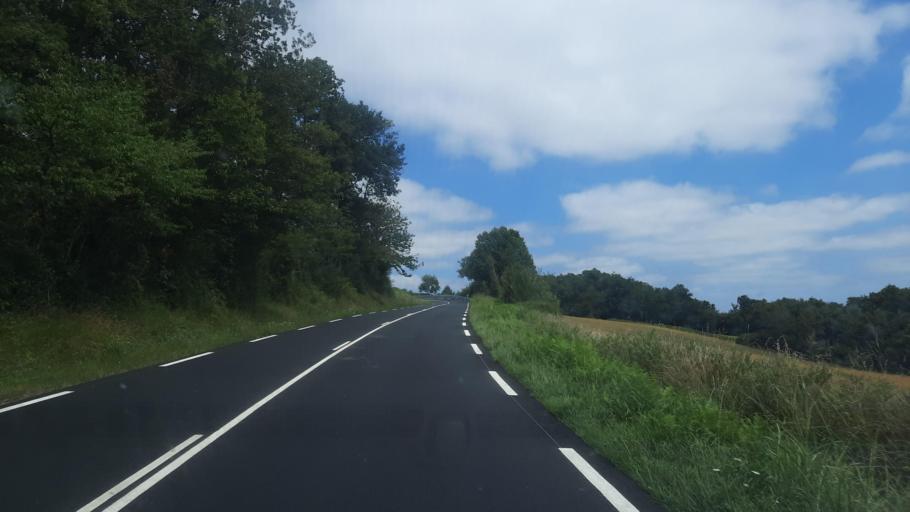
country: FR
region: Midi-Pyrenees
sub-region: Departement de la Haute-Garonne
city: Boulogne-sur-Gesse
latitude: 43.2933
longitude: 0.5797
